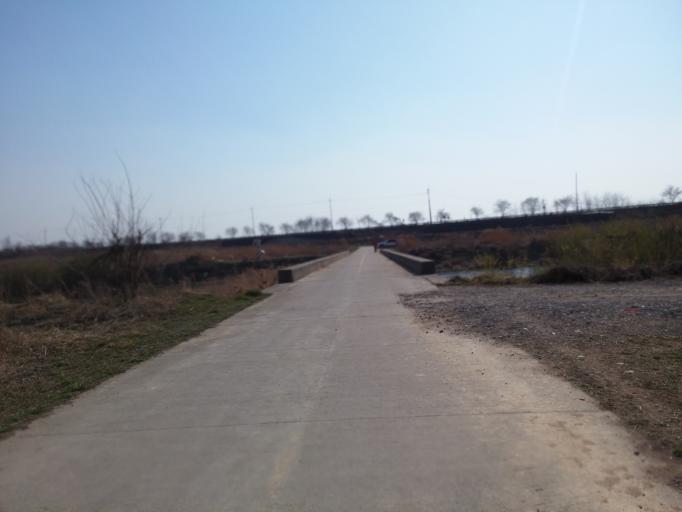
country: KR
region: Chungcheongbuk-do
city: Cheongju-si
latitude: 36.6289
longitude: 127.3500
